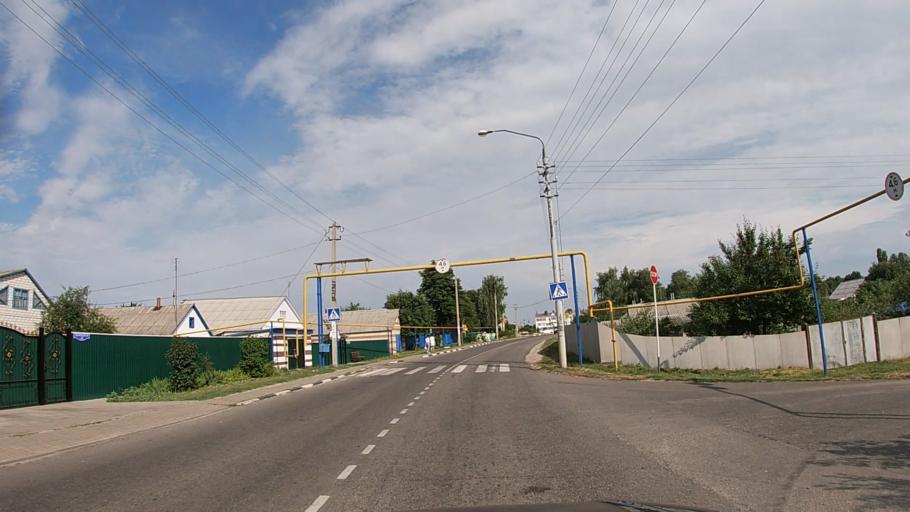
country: RU
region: Belgorod
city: Krasnaya Yaruga
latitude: 50.8005
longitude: 35.6612
